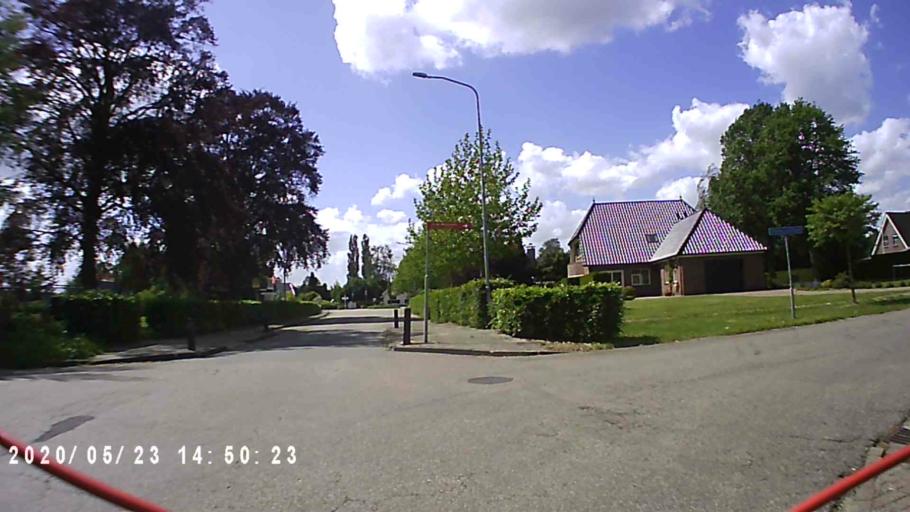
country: NL
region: Groningen
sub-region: Gemeente Delfzijl
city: Delfzijl
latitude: 53.2577
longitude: 6.9375
